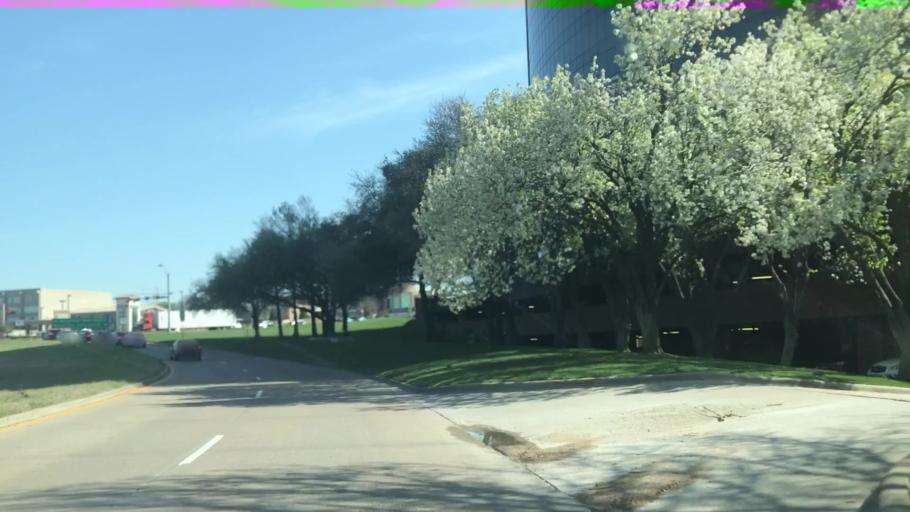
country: US
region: Texas
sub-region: Dallas County
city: Irving
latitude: 32.8897
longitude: -96.9650
